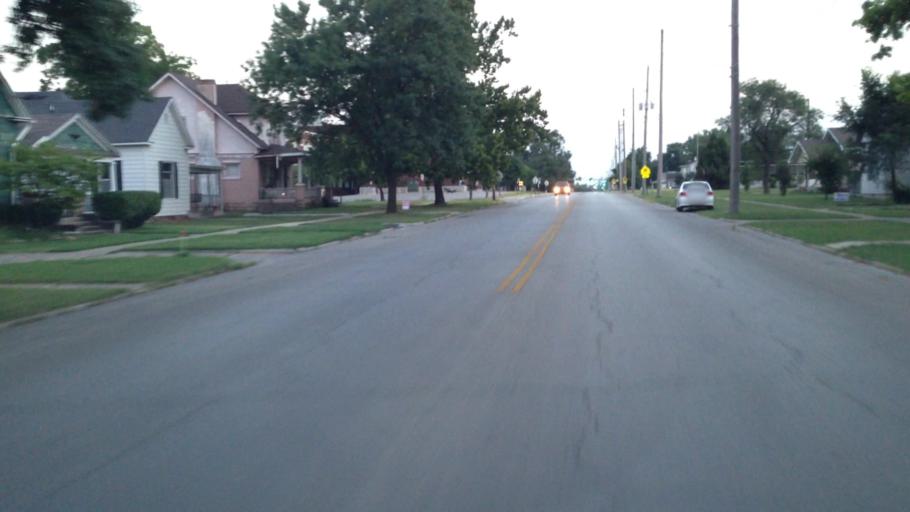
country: US
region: Kansas
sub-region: Montgomery County
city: Independence
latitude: 37.2298
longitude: -95.7108
